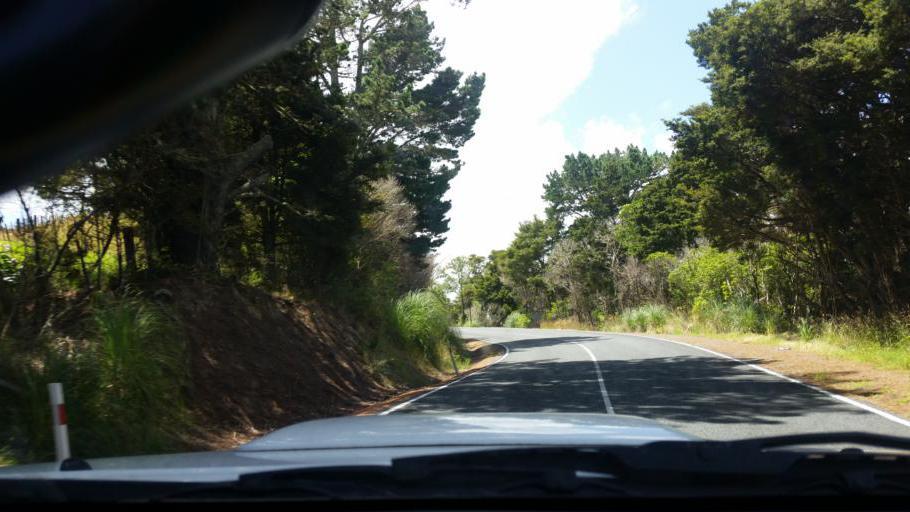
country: NZ
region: Northland
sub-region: Whangarei
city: Ruakaka
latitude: -36.0867
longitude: 174.2399
